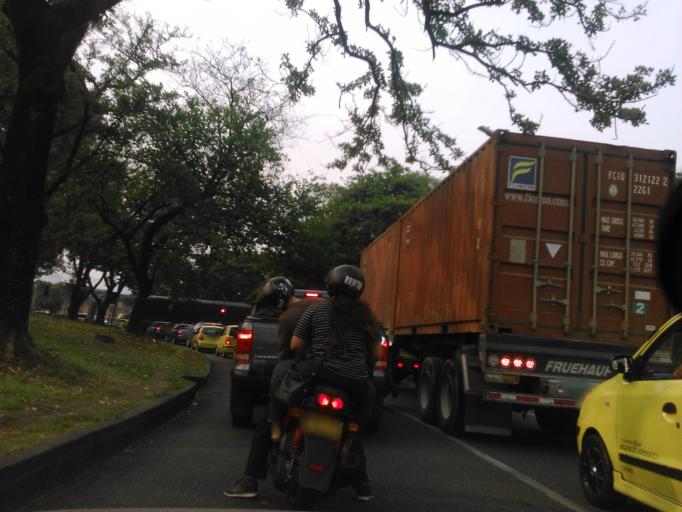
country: CO
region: Antioquia
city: Itagui
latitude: 6.1971
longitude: -75.5855
